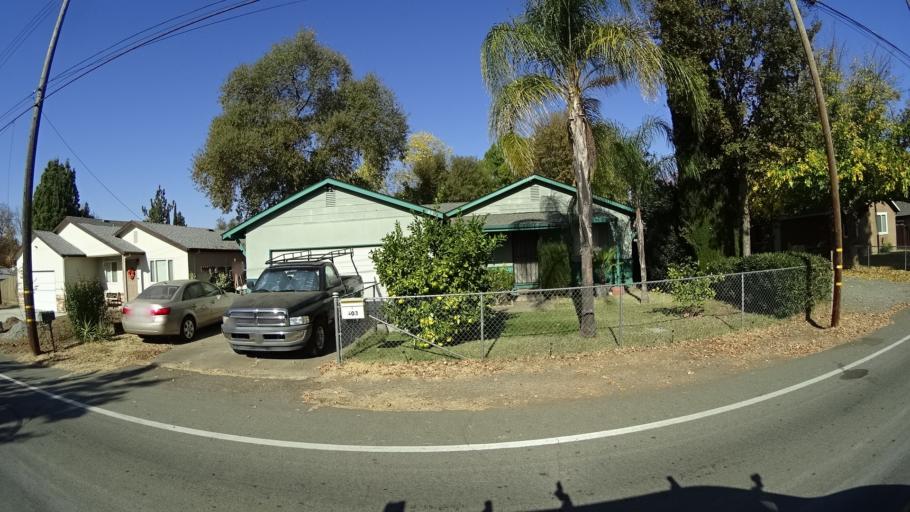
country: US
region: California
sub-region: Sacramento County
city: Citrus Heights
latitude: 38.7221
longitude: -121.2864
